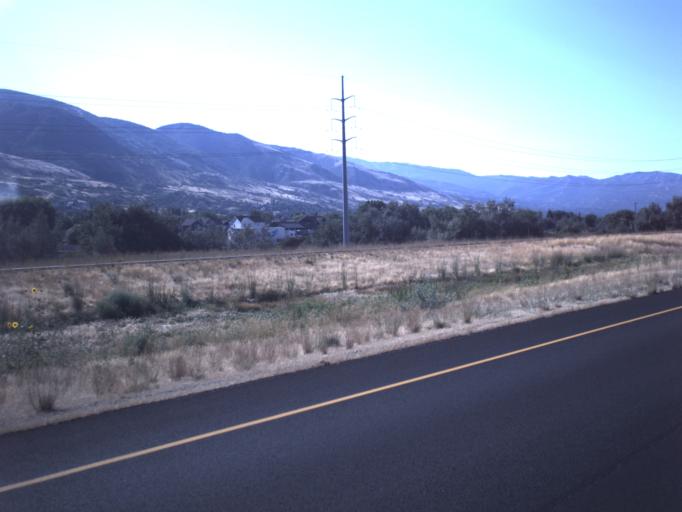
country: US
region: Utah
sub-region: Davis County
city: Farmington
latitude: 40.9544
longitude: -111.8932
